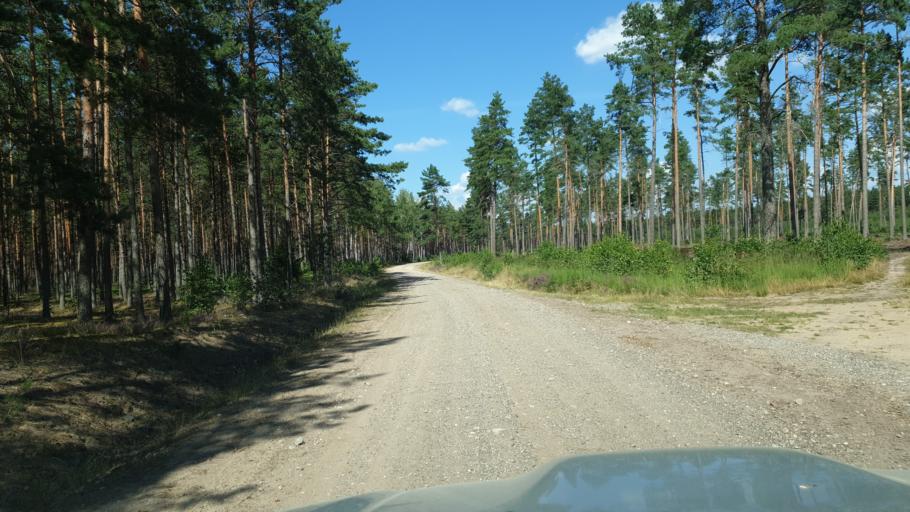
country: LT
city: Sirvintos
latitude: 54.8978
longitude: 24.9573
